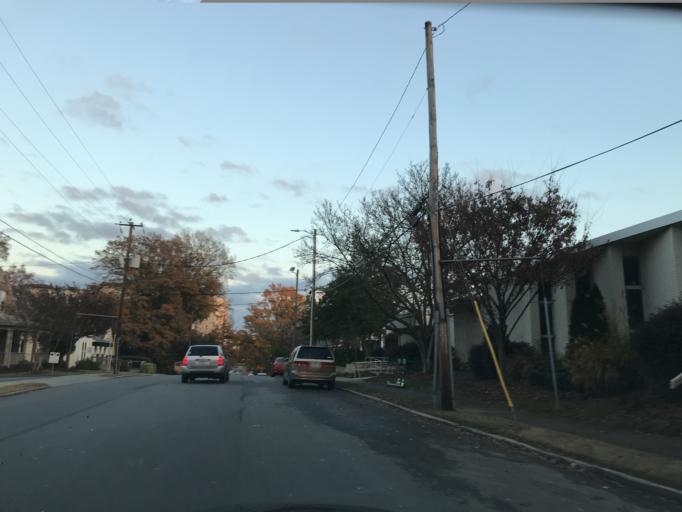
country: US
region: North Carolina
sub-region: Wake County
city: West Raleigh
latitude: 35.7850
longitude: -78.6506
